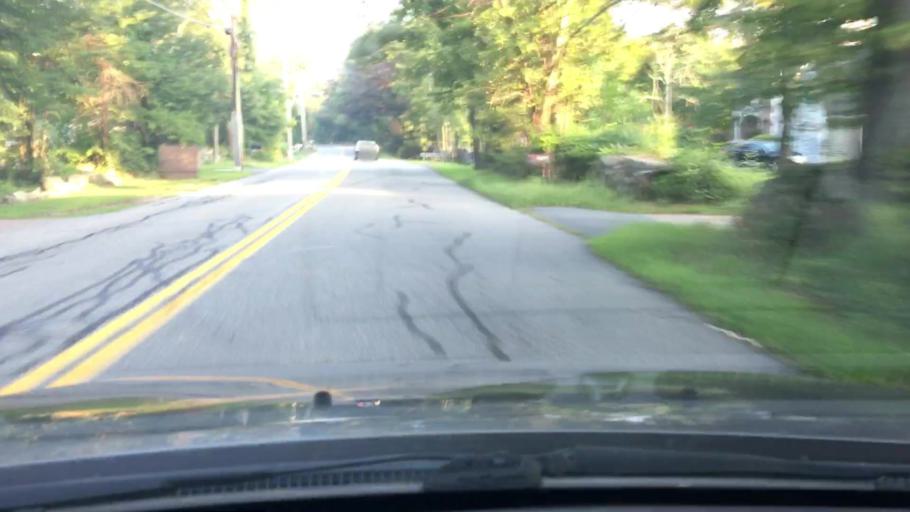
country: US
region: Massachusetts
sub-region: Worcester County
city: Hopedale
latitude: 42.1650
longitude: -71.5424
